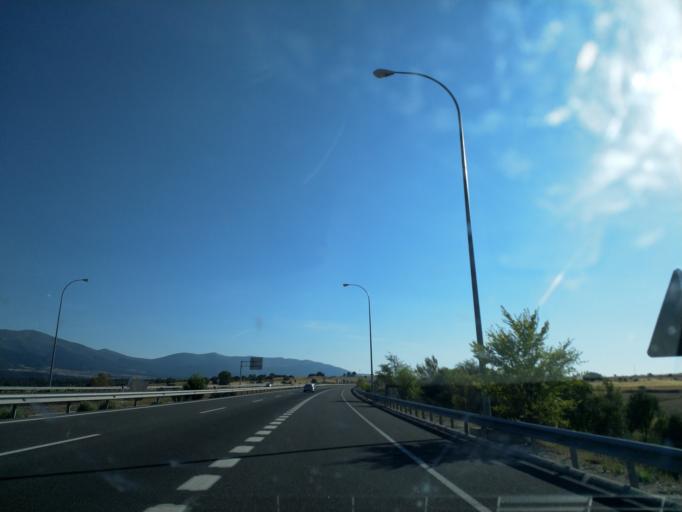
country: ES
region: Castille and Leon
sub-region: Provincia de Segovia
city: Segovia
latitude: 40.9006
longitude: -4.1057
